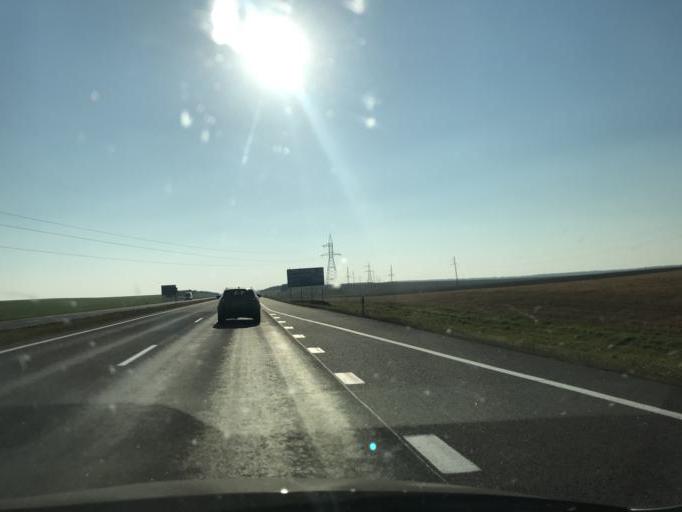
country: BY
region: Grodnenskaya
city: Mir
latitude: 53.4432
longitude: 26.5928
